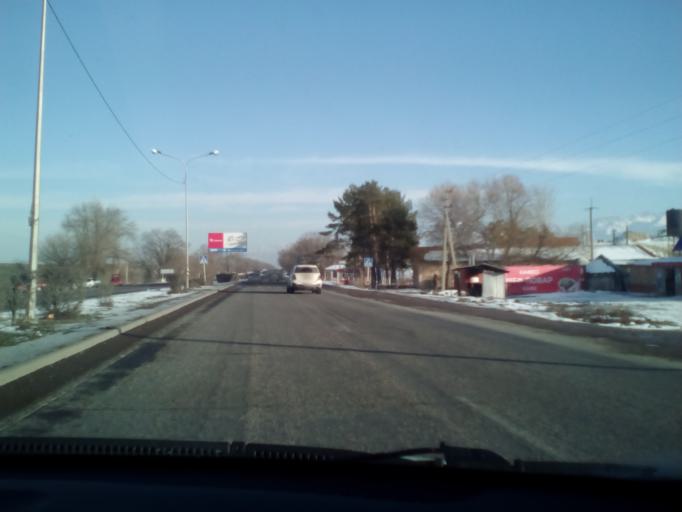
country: KZ
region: Almaty Oblysy
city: Burunday
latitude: 43.2224
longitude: 76.4258
